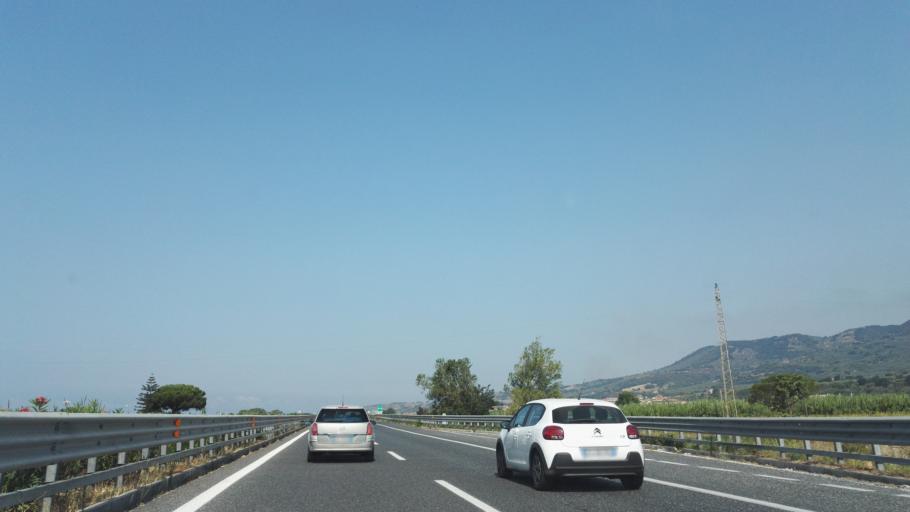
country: IT
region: Calabria
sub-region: Provincia di Catanzaro
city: Santa Eufemia Lamezia
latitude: 38.9328
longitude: 16.2245
